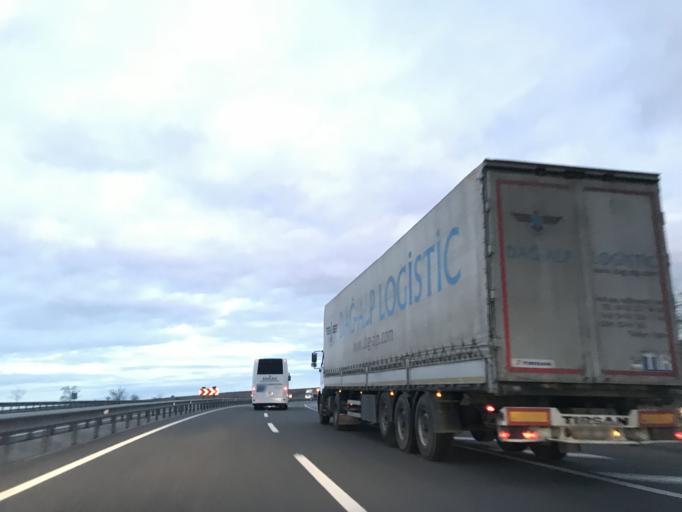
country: TR
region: Ankara
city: Altpinar
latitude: 39.2913
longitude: 32.9533
